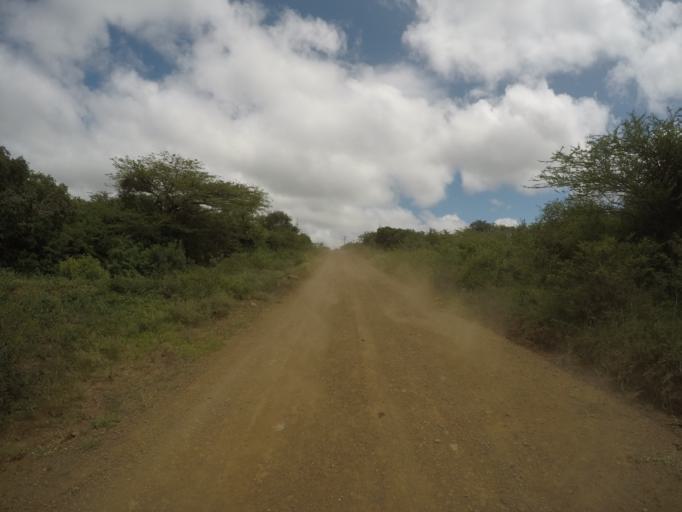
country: ZA
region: KwaZulu-Natal
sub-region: uThungulu District Municipality
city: Empangeni
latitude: -28.5710
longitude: 31.8254
